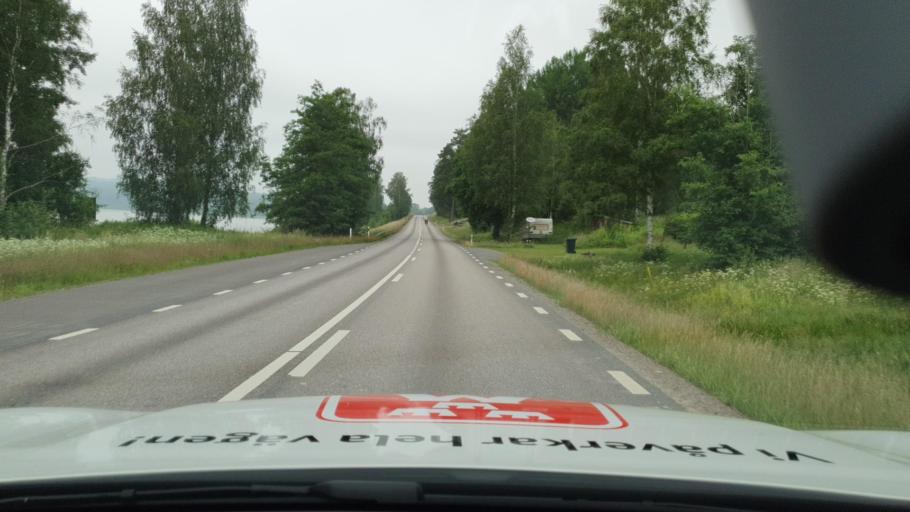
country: SE
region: Vaermland
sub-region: Karlstads Kommun
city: Edsvalla
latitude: 59.6287
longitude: 13.1615
